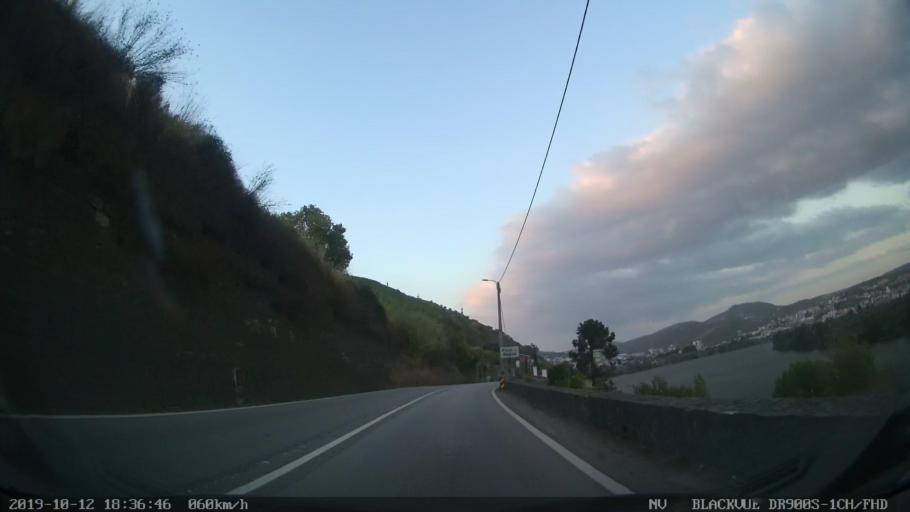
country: PT
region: Vila Real
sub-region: Peso da Regua
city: Godim
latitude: 41.1534
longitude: -7.8090
